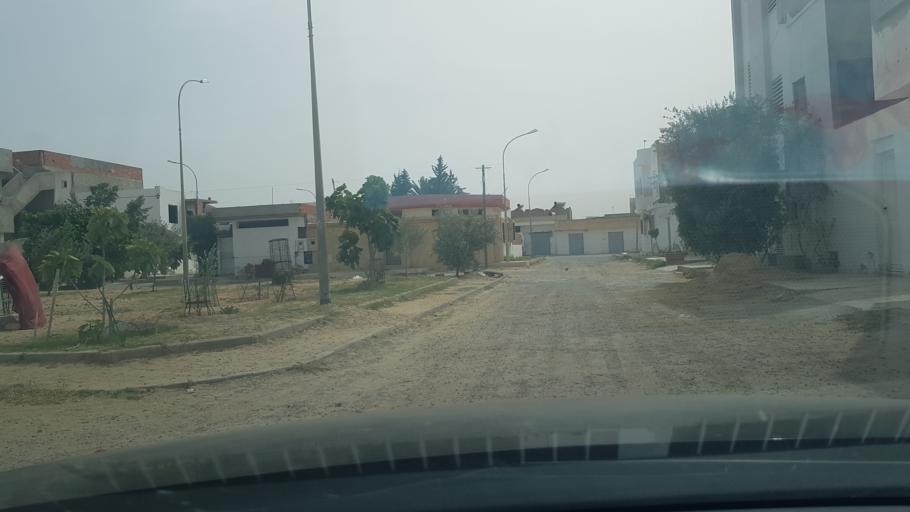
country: TN
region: Safaqis
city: Al Qarmadah
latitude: 34.8245
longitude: 10.7482
